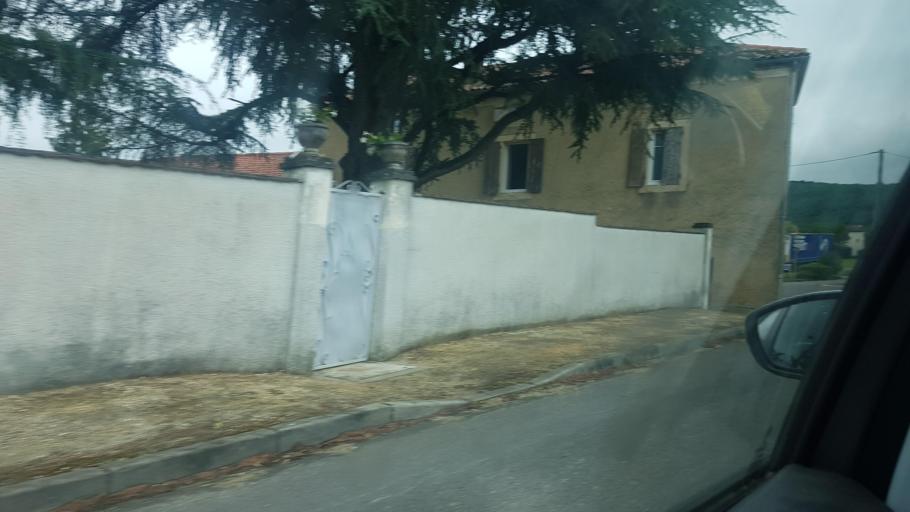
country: FR
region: Aquitaine
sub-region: Departement du Lot-et-Garonne
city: Montayral
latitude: 44.4929
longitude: 1.0829
